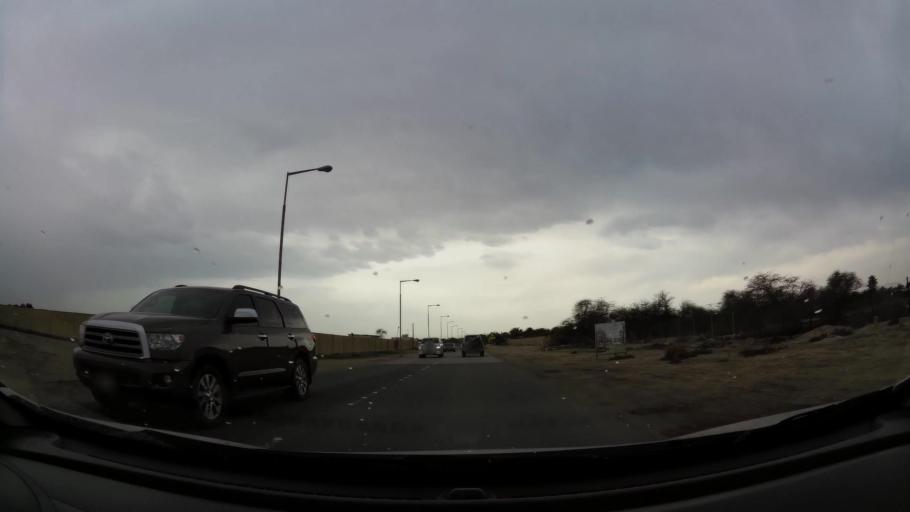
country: BH
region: Central Governorate
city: Madinat Hamad
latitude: 26.1643
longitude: 50.4577
